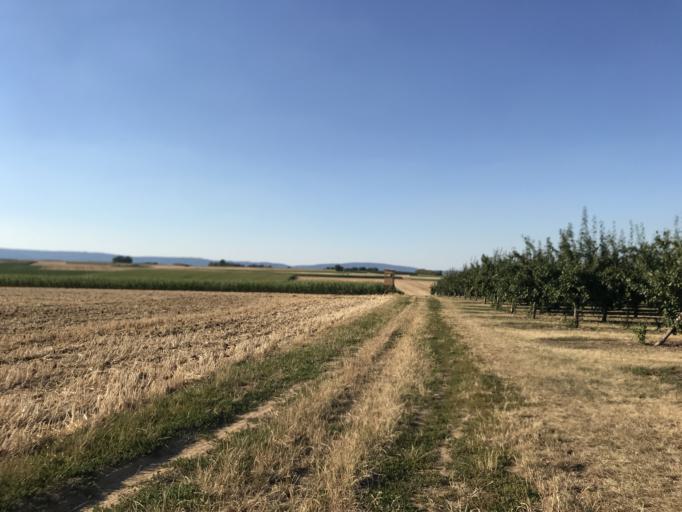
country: DE
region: Rheinland-Pfalz
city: Essenheim
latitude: 49.9432
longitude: 8.1371
